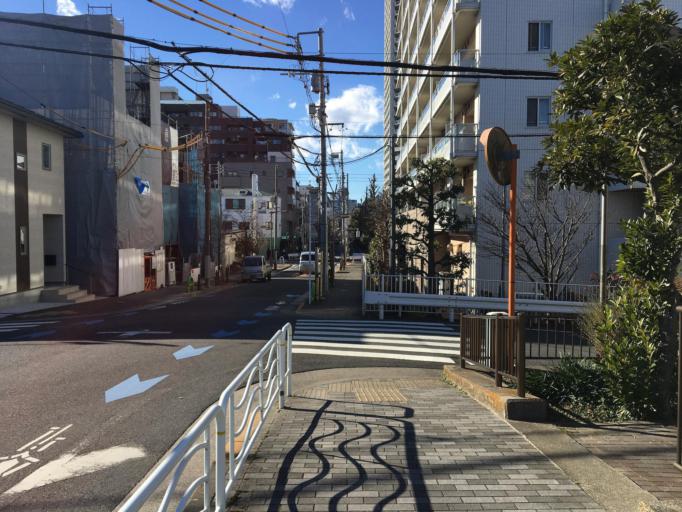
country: JP
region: Tokyo
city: Urayasu
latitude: 35.6816
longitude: 139.8100
